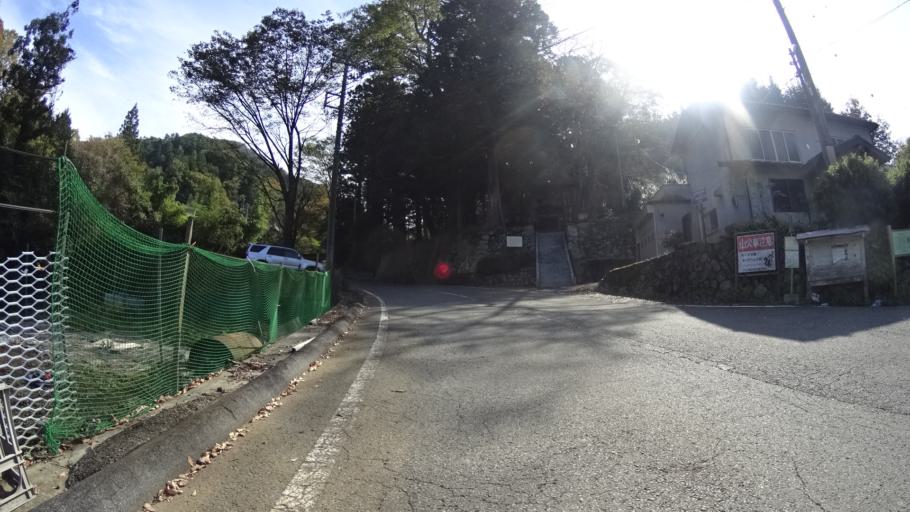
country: JP
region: Yamanashi
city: Otsuki
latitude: 35.5851
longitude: 138.9669
